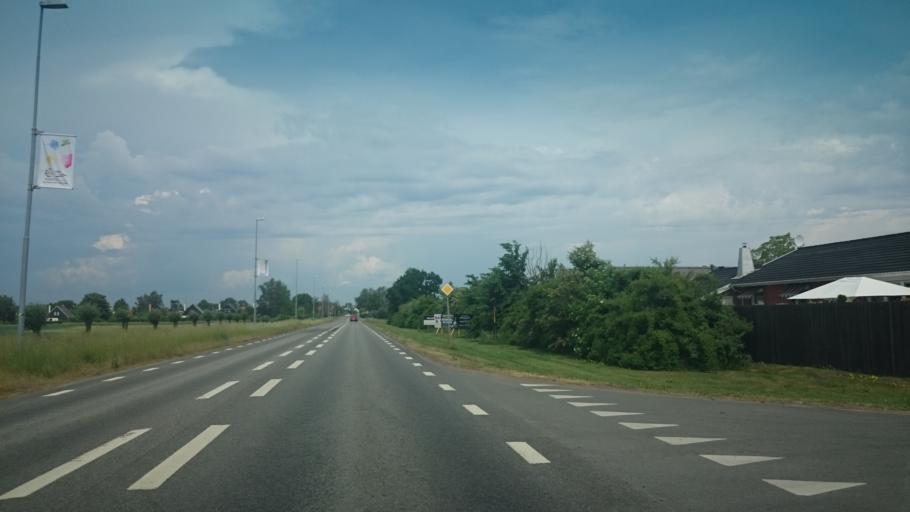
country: SE
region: Skane
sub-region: Kristianstads Kommun
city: Norra Asum
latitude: 56.0057
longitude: 14.1515
